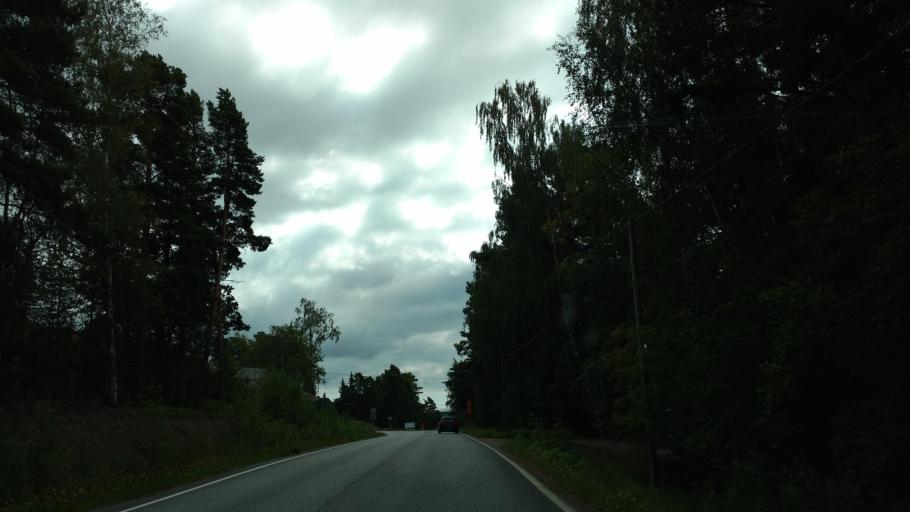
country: FI
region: Varsinais-Suomi
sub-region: Aboland-Turunmaa
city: Dragsfjaerd
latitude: 59.9890
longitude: 22.4516
